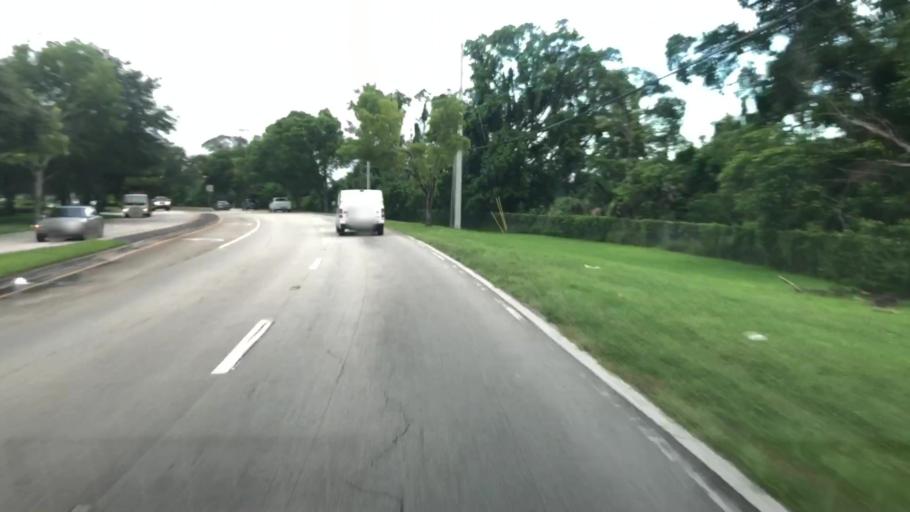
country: US
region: Florida
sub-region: Broward County
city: Twin Lakes
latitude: 26.1845
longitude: -80.1742
